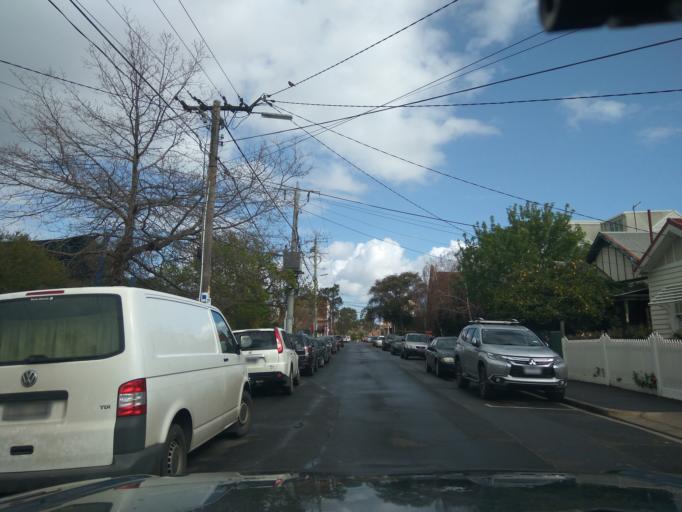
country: AU
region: Victoria
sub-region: Maribyrnong
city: Yarraville
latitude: -37.8173
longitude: 144.8919
